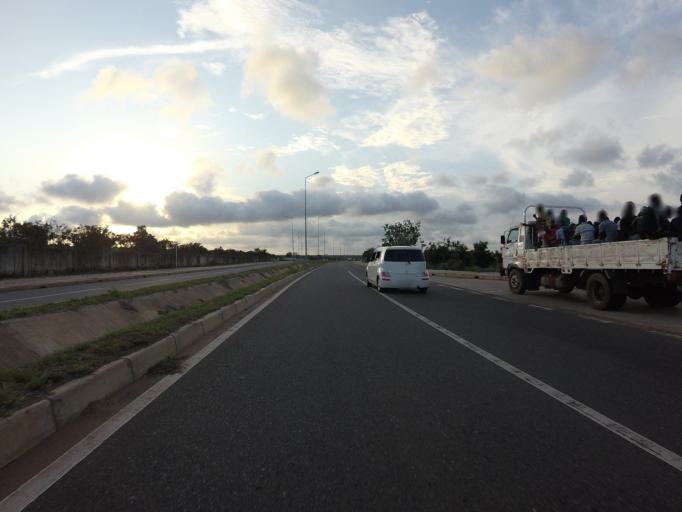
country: GH
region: Greater Accra
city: Teshi Old Town
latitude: 5.6115
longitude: -0.1484
